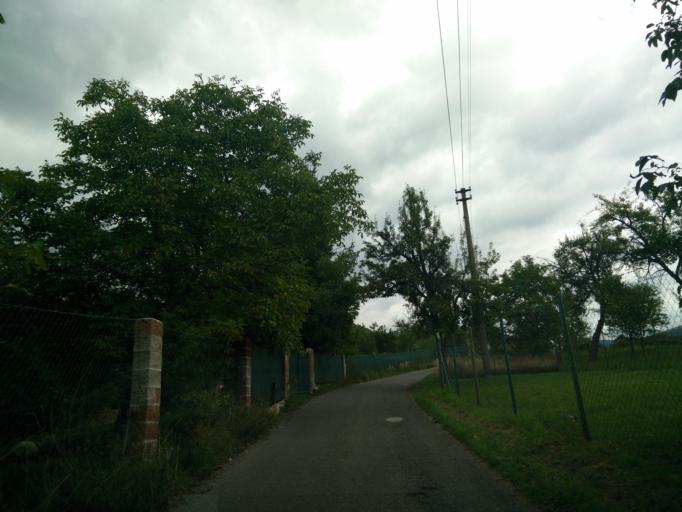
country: SK
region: Nitriansky
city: Novaky
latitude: 48.6018
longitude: 18.5122
